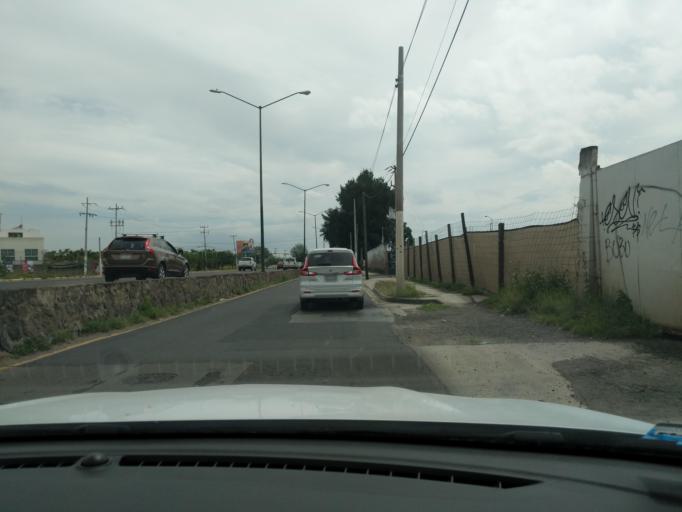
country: MX
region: Jalisco
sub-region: Zapopan
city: Puerta del Llano
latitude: 20.7856
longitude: -103.4688
